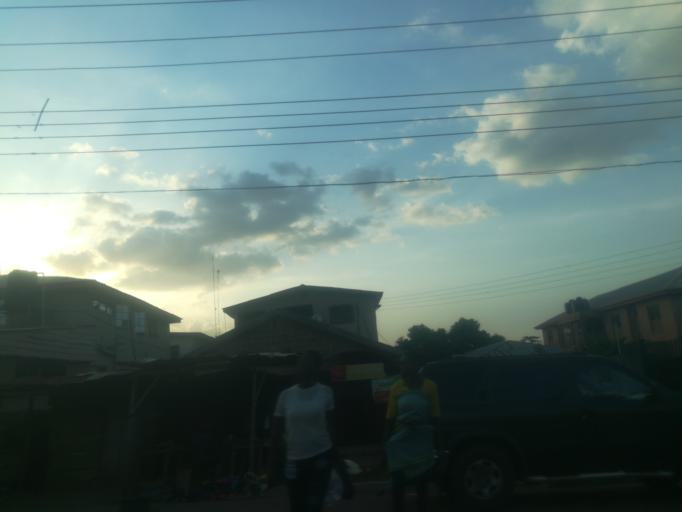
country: NG
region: Ogun
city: Abeokuta
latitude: 7.1454
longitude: 3.3385
